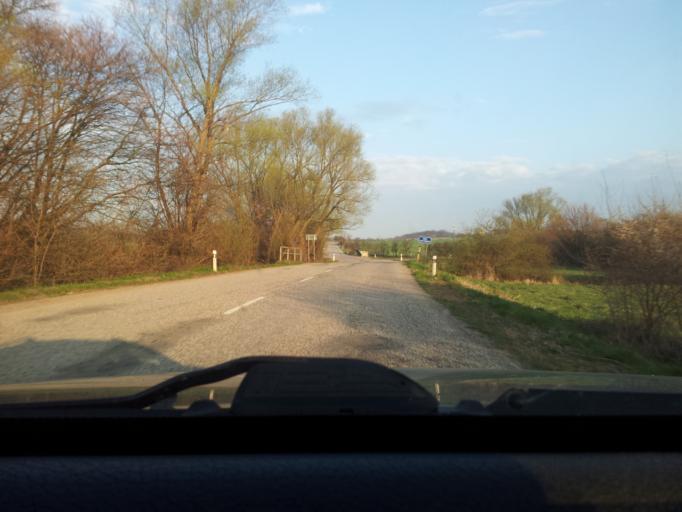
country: SK
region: Nitriansky
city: Tlmace
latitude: 48.2815
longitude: 18.4748
